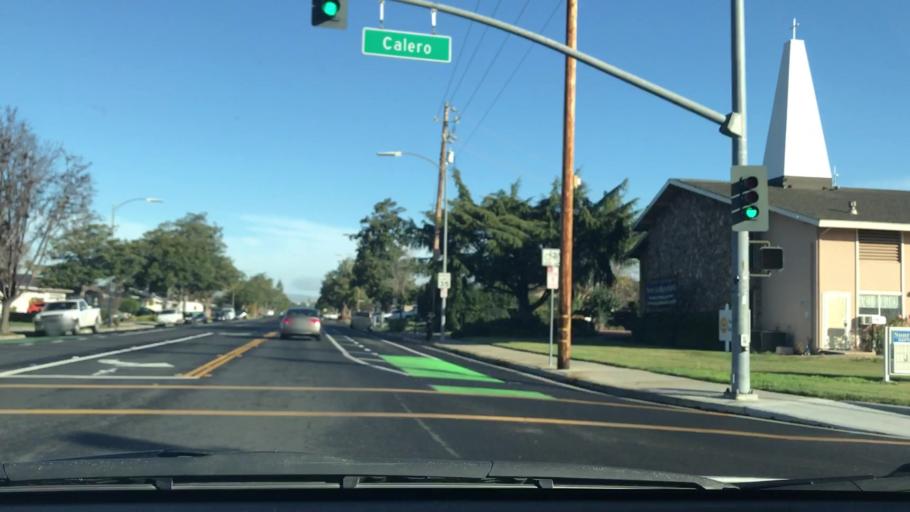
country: US
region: California
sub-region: Santa Clara County
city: Seven Trees
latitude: 37.2421
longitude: -121.8397
